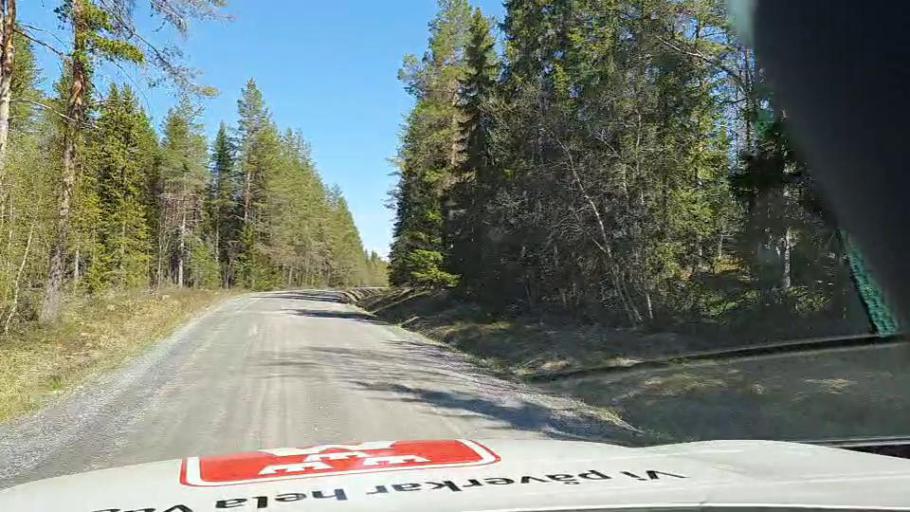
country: SE
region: Jaemtland
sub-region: Krokoms Kommun
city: Valla
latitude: 63.6661
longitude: 13.6792
